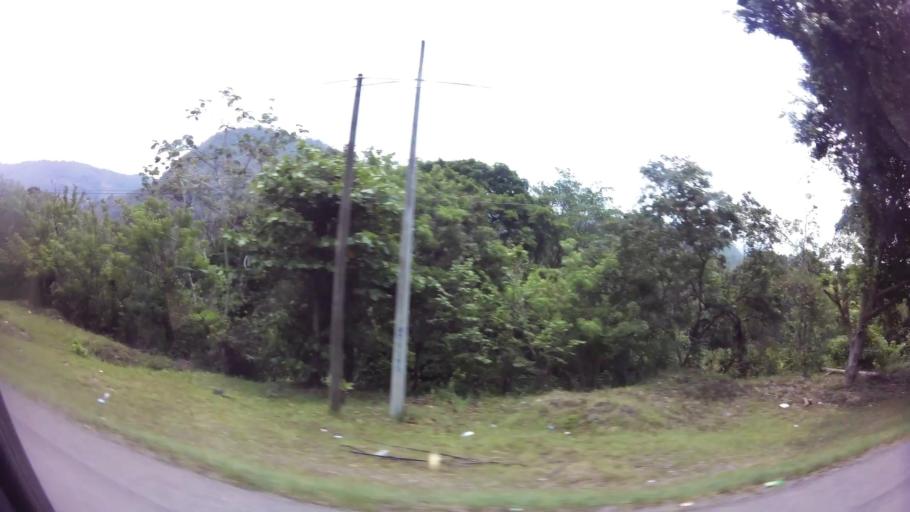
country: HN
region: Comayagua
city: Taulabe
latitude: 14.7251
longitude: -87.9649
